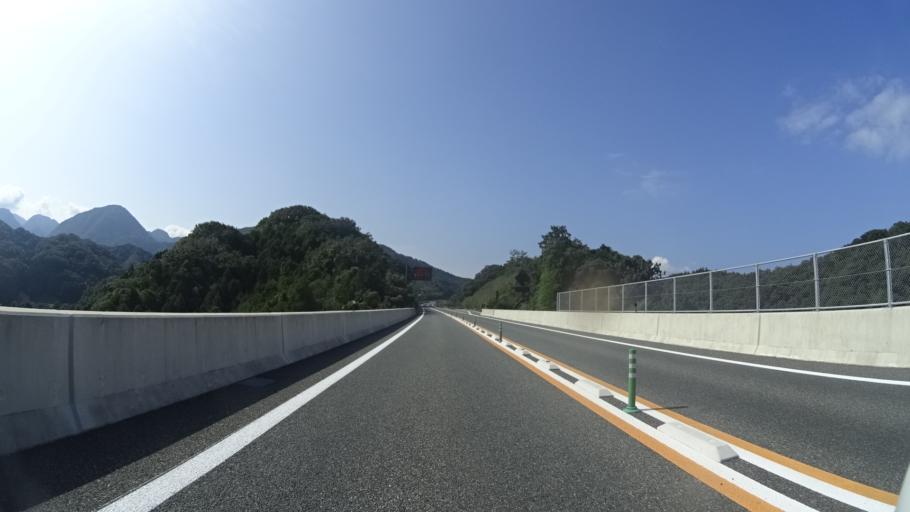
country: JP
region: Shimane
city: Odacho-oda
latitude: 35.1046
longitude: 132.3794
